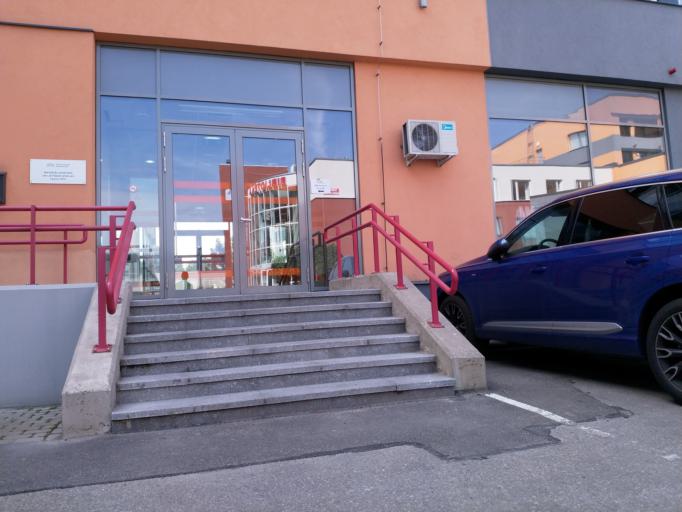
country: LV
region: Riga
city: Riga
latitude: 56.9533
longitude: 24.0791
